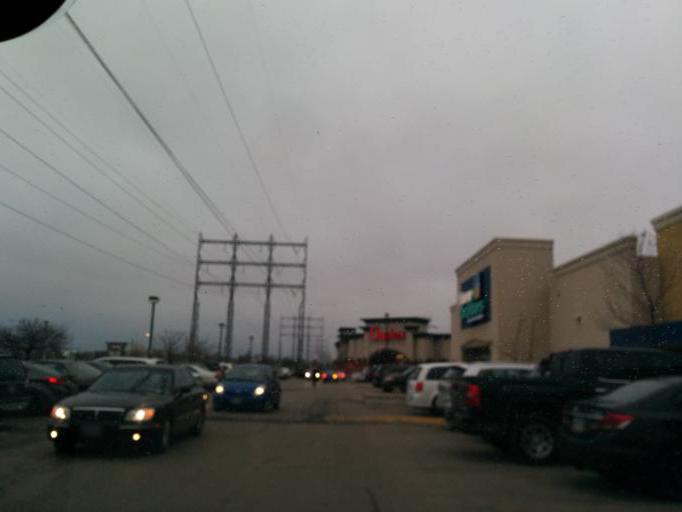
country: CA
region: Ontario
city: Etobicoke
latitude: 43.6150
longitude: -79.5604
